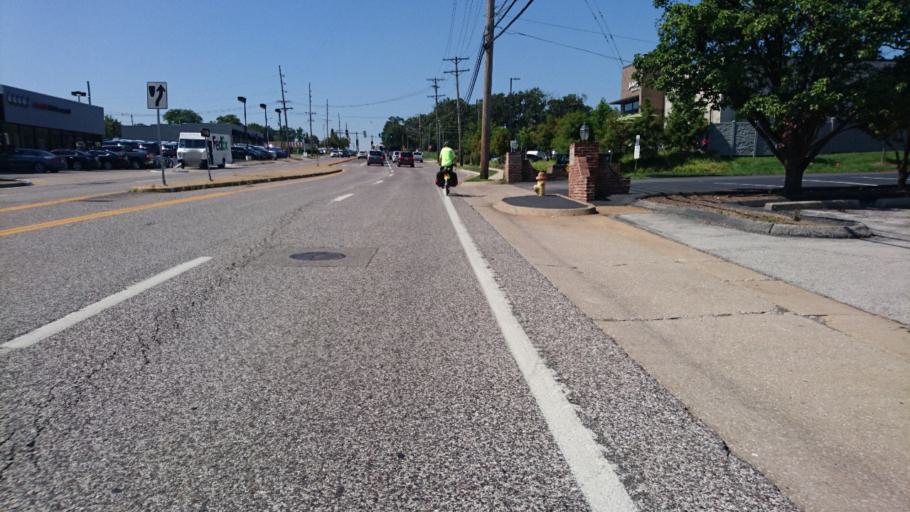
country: US
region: Missouri
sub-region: Saint Louis County
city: Warson Woods
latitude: 38.6008
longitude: -90.3949
